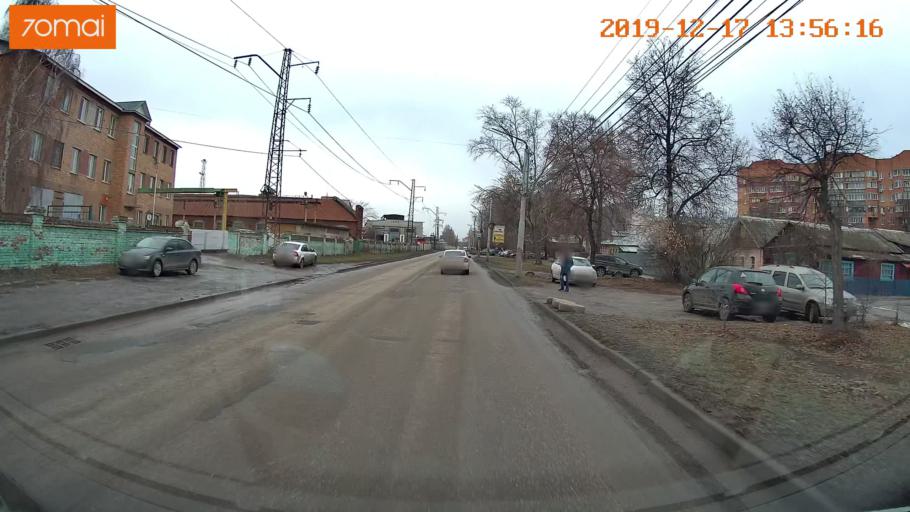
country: RU
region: Rjazan
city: Ryazan'
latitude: 54.6290
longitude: 39.6988
